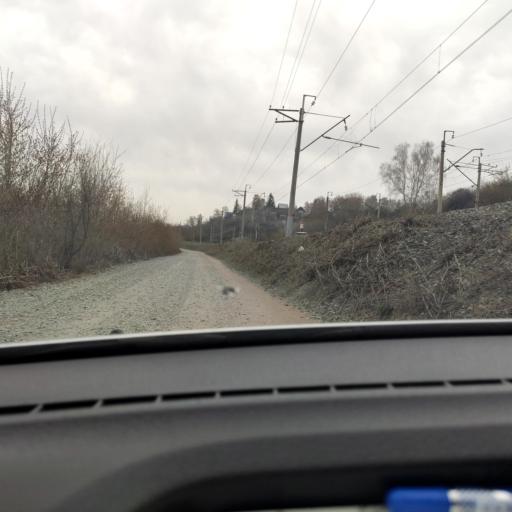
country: RU
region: Bashkortostan
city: Avdon
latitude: 54.6187
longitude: 55.6041
